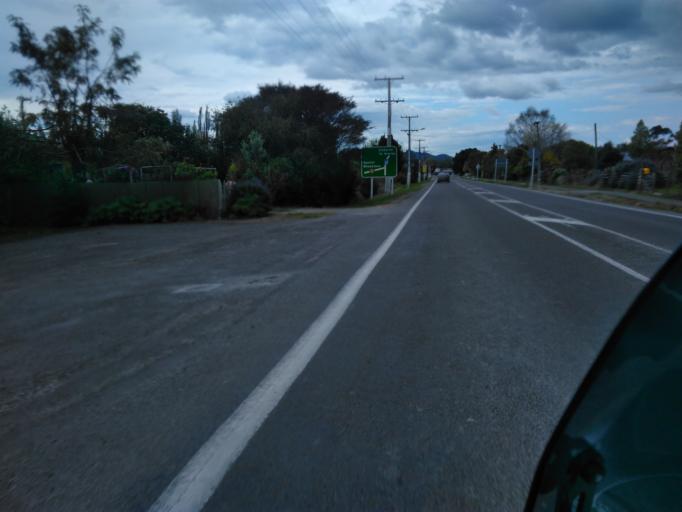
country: NZ
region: Gisborne
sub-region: Gisborne District
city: Gisborne
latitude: -38.6514
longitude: 177.9608
